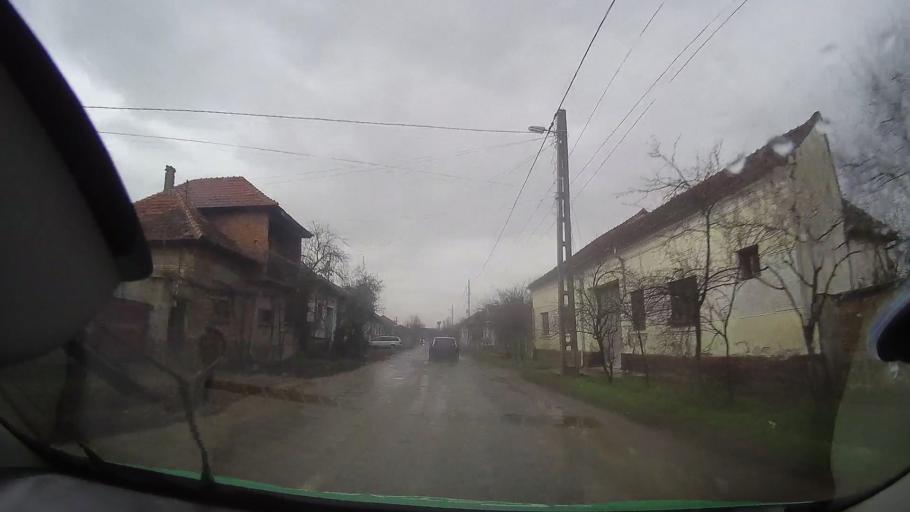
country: RO
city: Capalna
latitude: 46.7120
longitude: 22.0834
